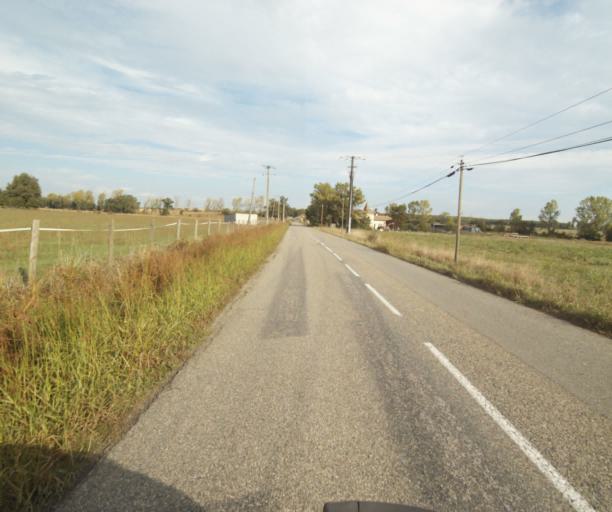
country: FR
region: Midi-Pyrenees
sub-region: Departement du Tarn-et-Garonne
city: Montech
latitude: 43.9723
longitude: 1.2327
